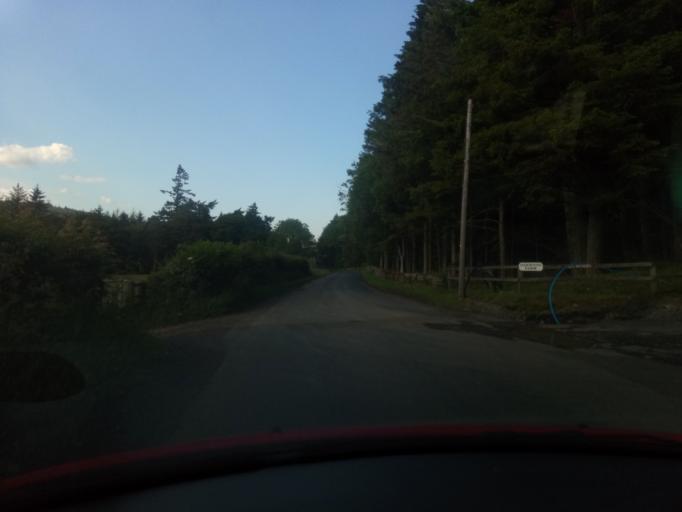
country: GB
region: Scotland
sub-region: The Scottish Borders
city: Selkirk
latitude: 55.5230
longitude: -2.9235
